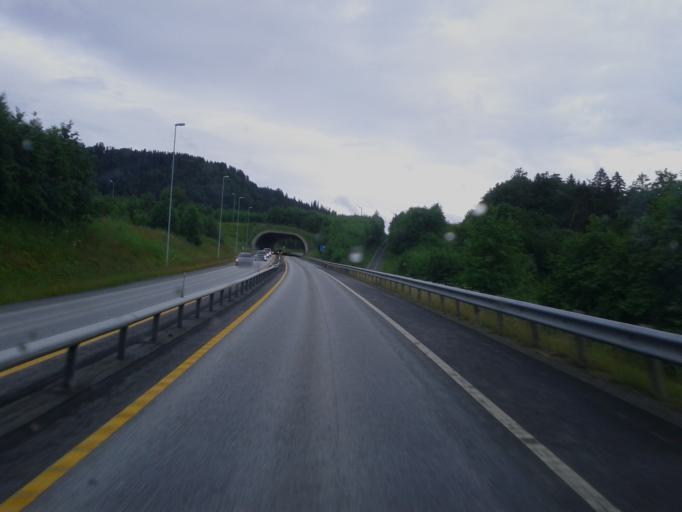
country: NO
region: Sor-Trondelag
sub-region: Melhus
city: Melhus
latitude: 63.2579
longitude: 10.2832
